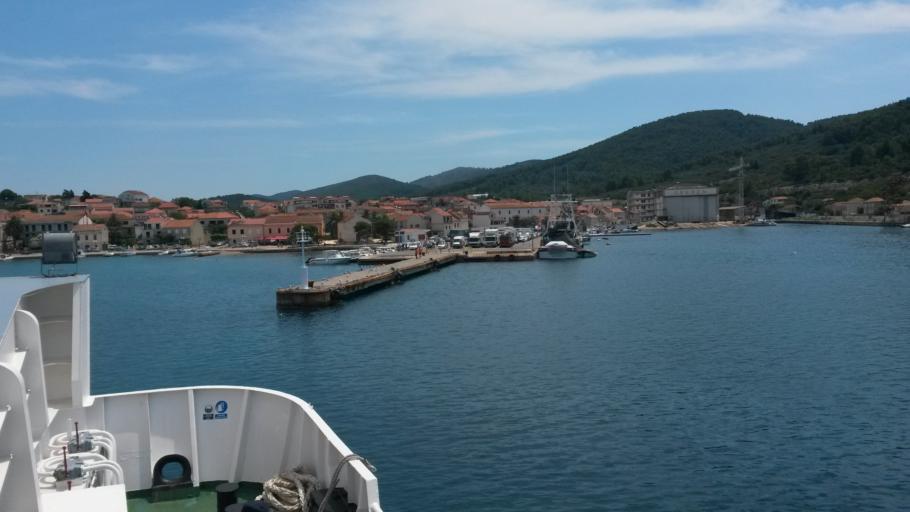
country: HR
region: Dubrovacko-Neretvanska
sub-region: Grad Dubrovnik
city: Vela Luka
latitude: 42.9602
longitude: 16.7092
